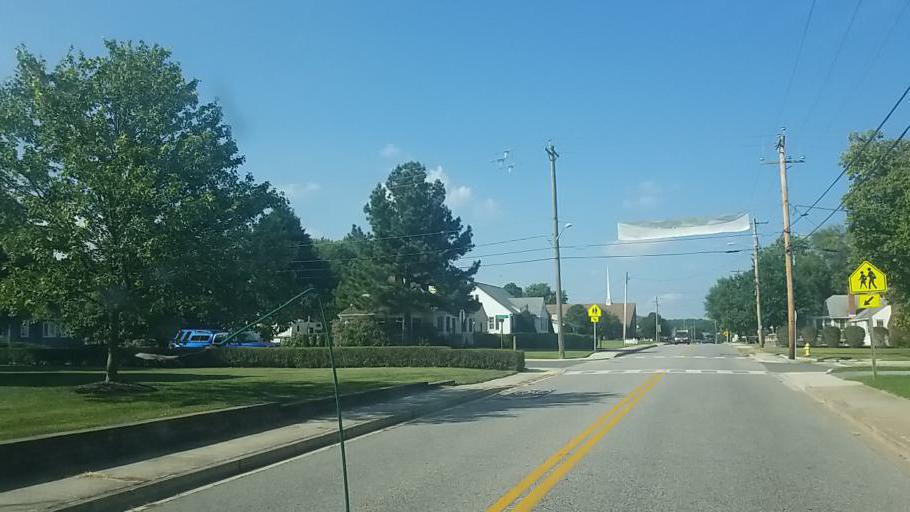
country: US
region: Maryland
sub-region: Worcester County
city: Berlin
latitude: 38.3315
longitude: -75.2144
